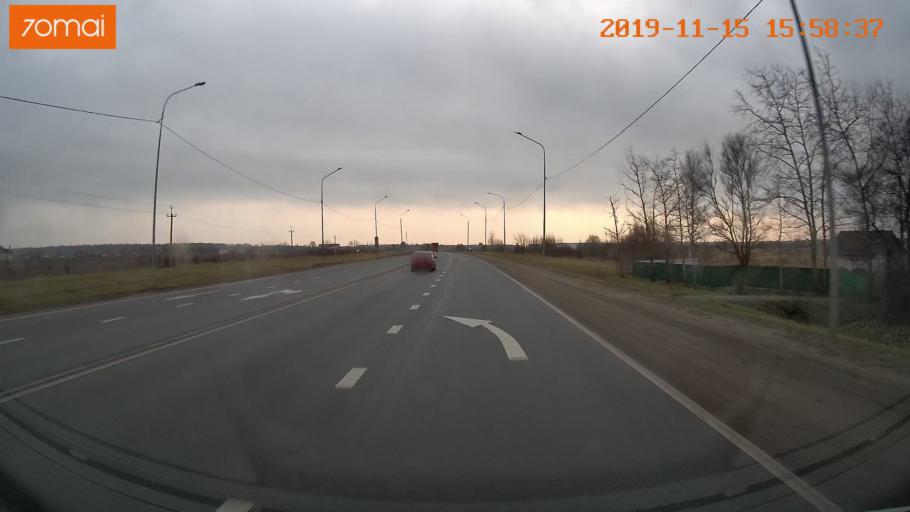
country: RU
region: Jaroslavl
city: Yaroslavl
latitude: 57.8176
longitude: 39.9533
